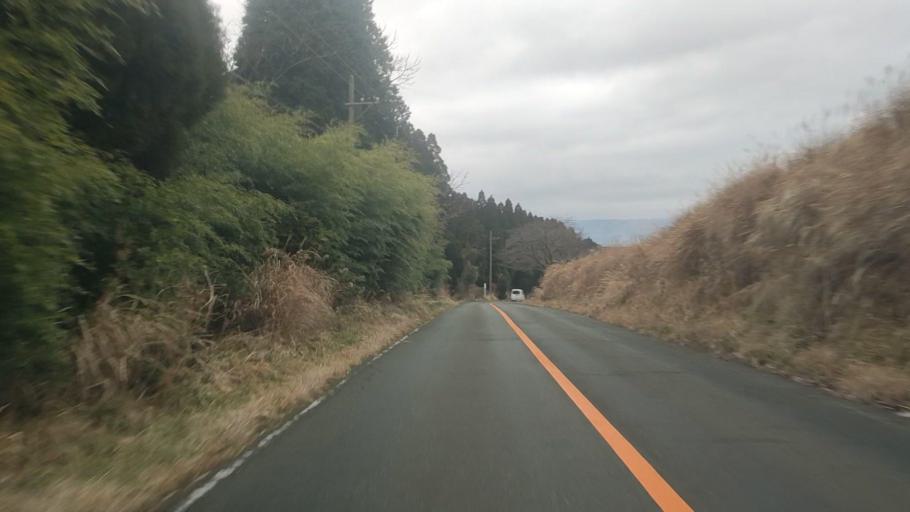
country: JP
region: Kumamoto
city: Aso
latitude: 32.9096
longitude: 131.1356
